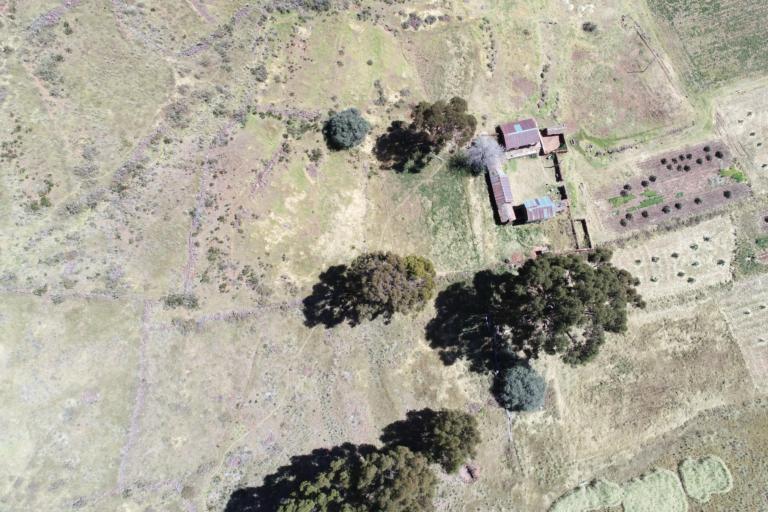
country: BO
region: La Paz
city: Tiahuanaco
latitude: -16.6036
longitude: -68.7735
